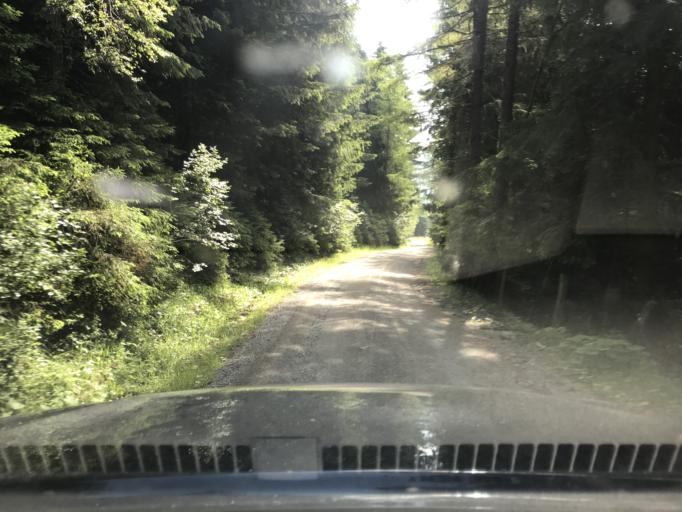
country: AT
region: Styria
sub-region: Politischer Bezirk Murau
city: Sankt Peter am Kammersberg
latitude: 47.2213
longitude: 14.1775
